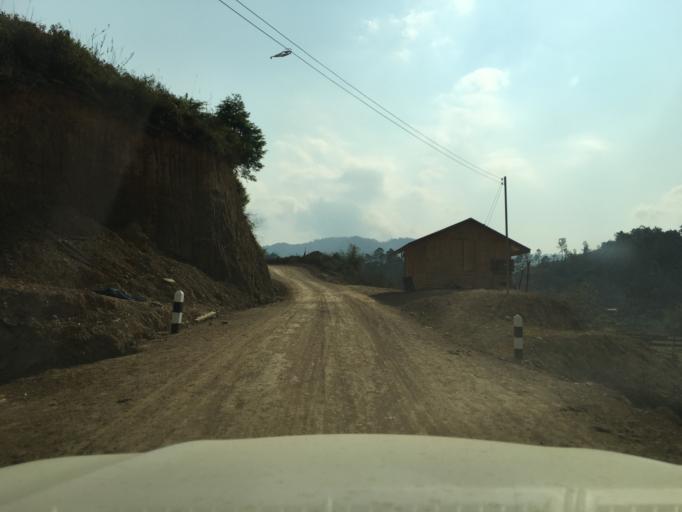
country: LA
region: Houaphan
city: Huameung
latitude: 20.2060
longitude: 103.8332
